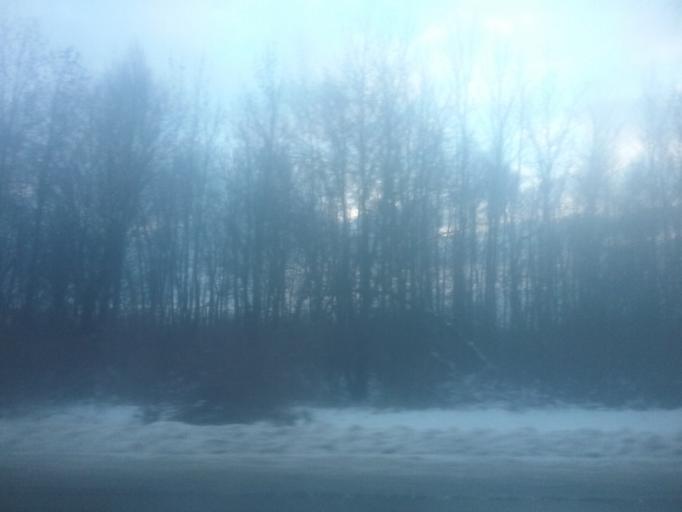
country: RU
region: Tula
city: Shvartsevskiy
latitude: 54.0252
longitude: 37.9652
